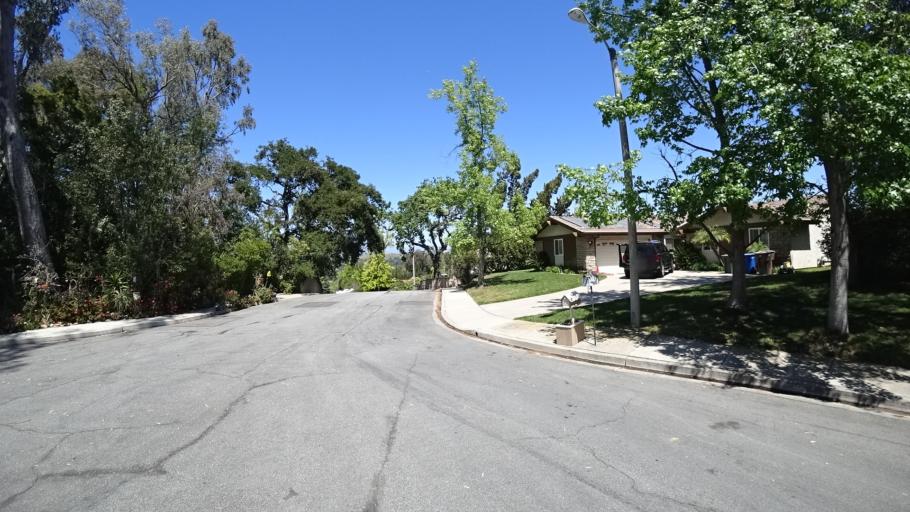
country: US
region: California
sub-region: Ventura County
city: Casa Conejo
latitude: 34.1740
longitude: -118.8970
